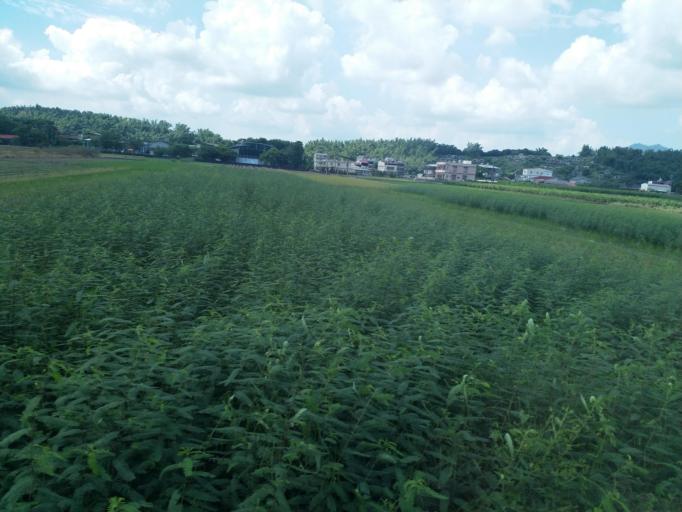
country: TW
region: Taiwan
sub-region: Pingtung
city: Pingtung
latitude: 22.8783
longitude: 120.5750
